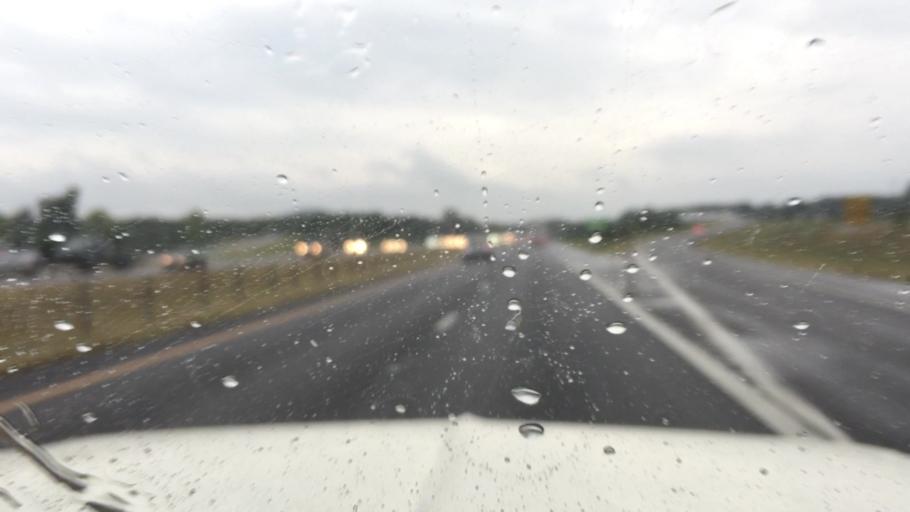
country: US
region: Alabama
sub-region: Morgan County
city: Hartselle
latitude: 34.4160
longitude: -86.8987
